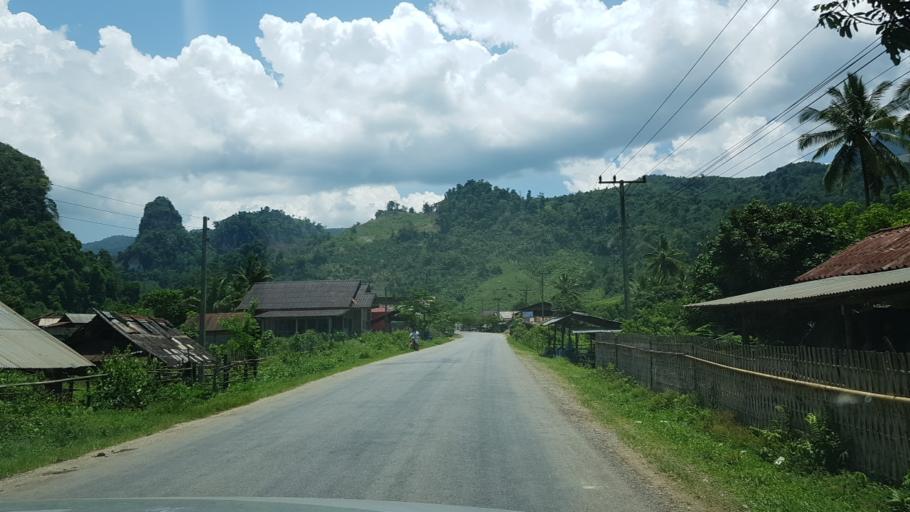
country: LA
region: Vientiane
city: Muang Kasi
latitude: 19.1248
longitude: 102.2520
